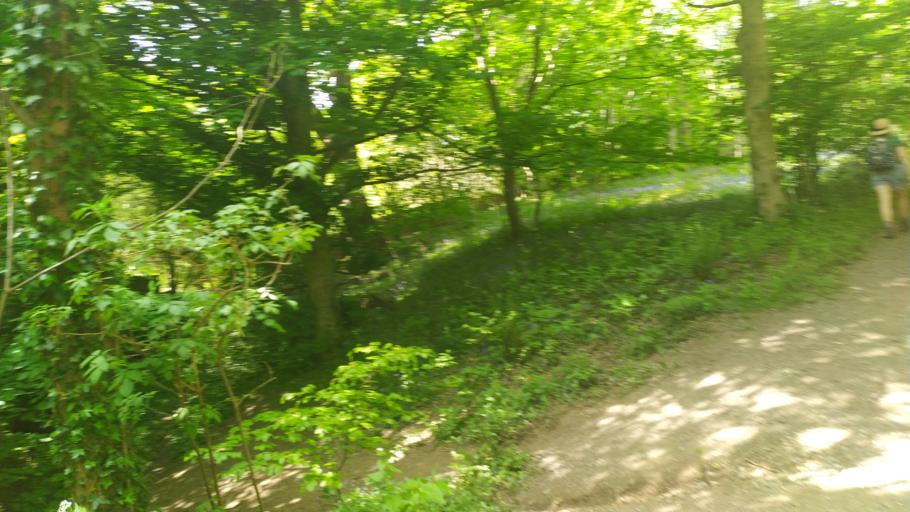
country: GB
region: England
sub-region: City and Borough of Leeds
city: Chapel Allerton
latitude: 53.8861
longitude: -1.5350
